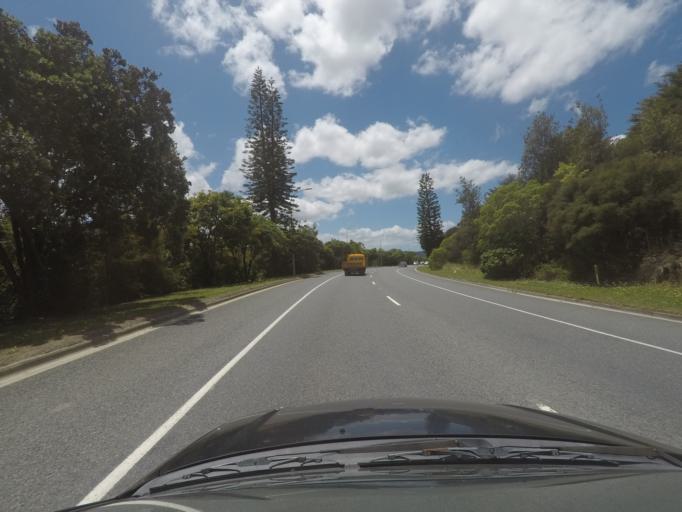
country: NZ
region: Northland
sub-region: Whangarei
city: Whangarei
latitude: -35.7468
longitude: 174.3213
